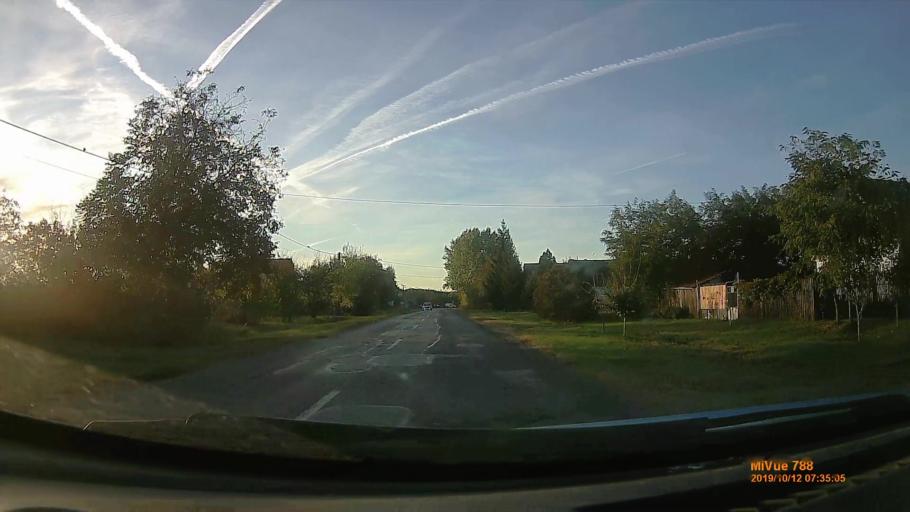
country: HU
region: Hajdu-Bihar
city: Pocsaj
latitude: 47.2565
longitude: 21.8105
